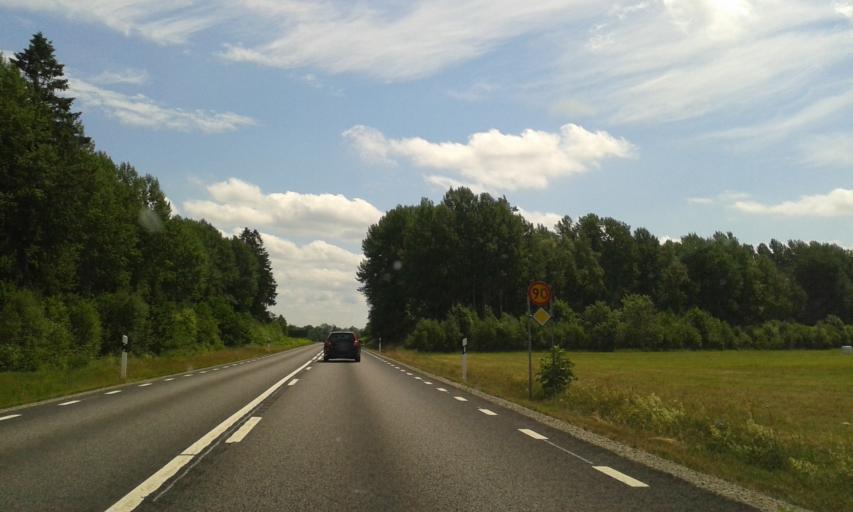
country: SE
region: Joenkoeping
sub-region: Varnamo Kommun
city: Rydaholm
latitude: 57.0009
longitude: 14.2754
